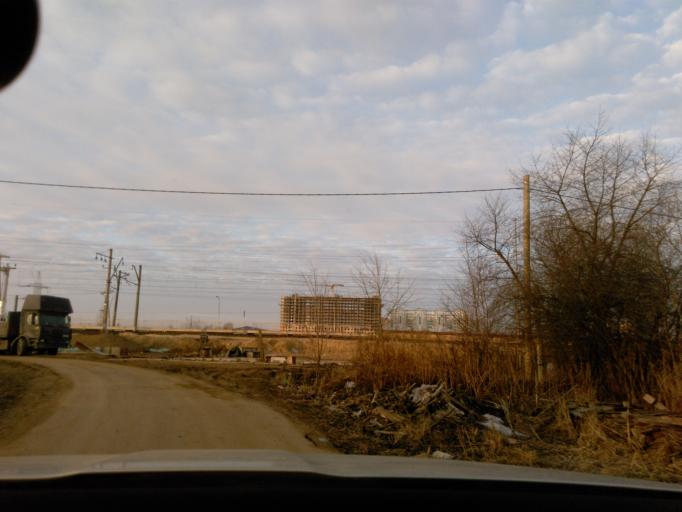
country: RU
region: Moskovskaya
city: Novopodrezkovo
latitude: 55.9257
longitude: 37.3797
